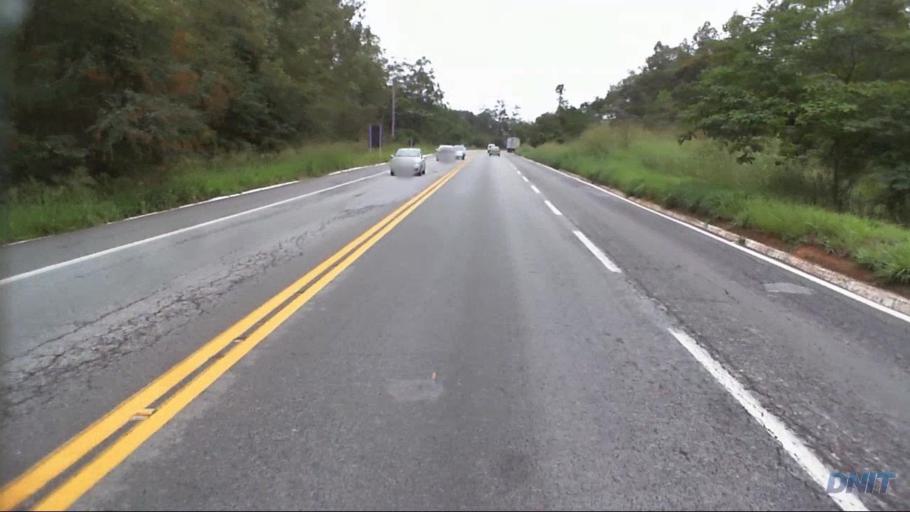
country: BR
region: Minas Gerais
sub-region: Joao Monlevade
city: Joao Monlevade
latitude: -19.8498
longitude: -43.2766
